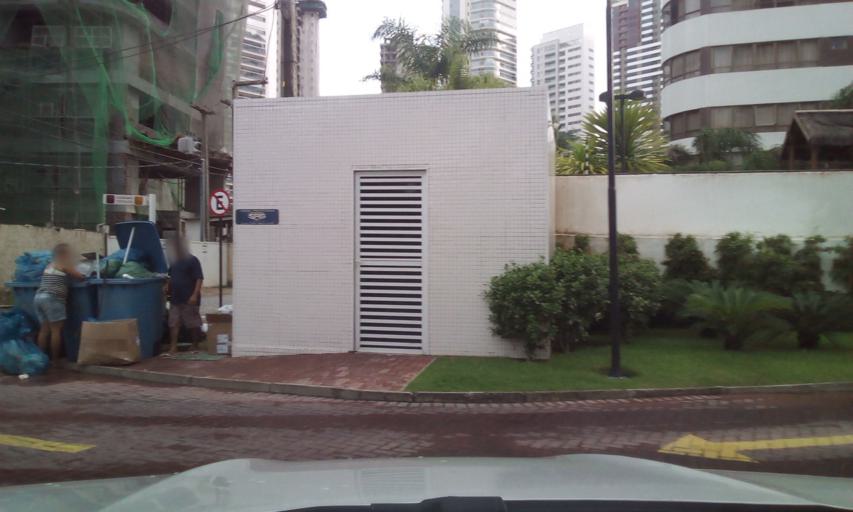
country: BR
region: Paraiba
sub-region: Joao Pessoa
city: Joao Pessoa
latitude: -7.1299
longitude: -34.8275
